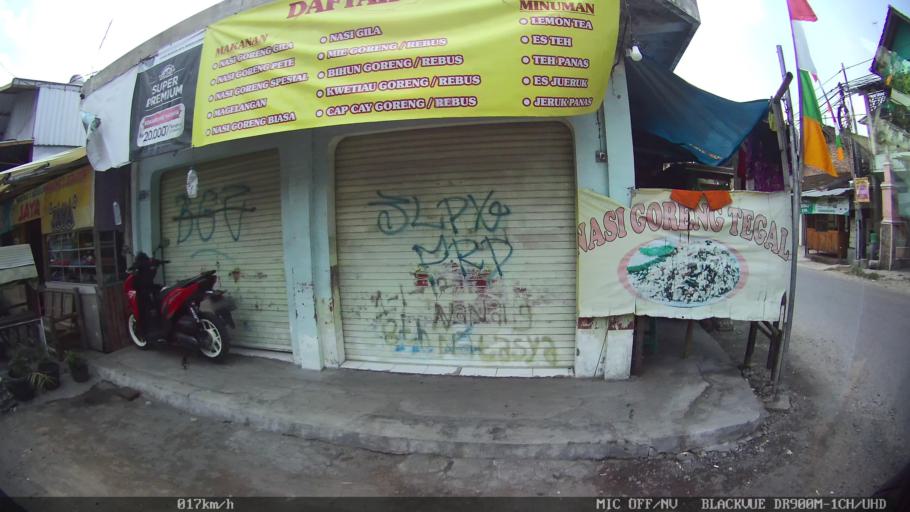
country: ID
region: Daerah Istimewa Yogyakarta
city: Yogyakarta
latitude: -7.8280
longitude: 110.4056
